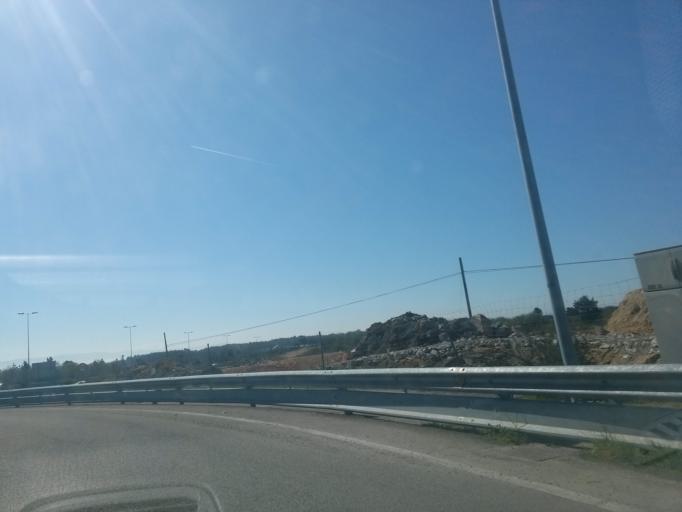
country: ES
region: Galicia
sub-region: Provincia de Lugo
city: Lugo
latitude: 43.0205
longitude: -7.5260
